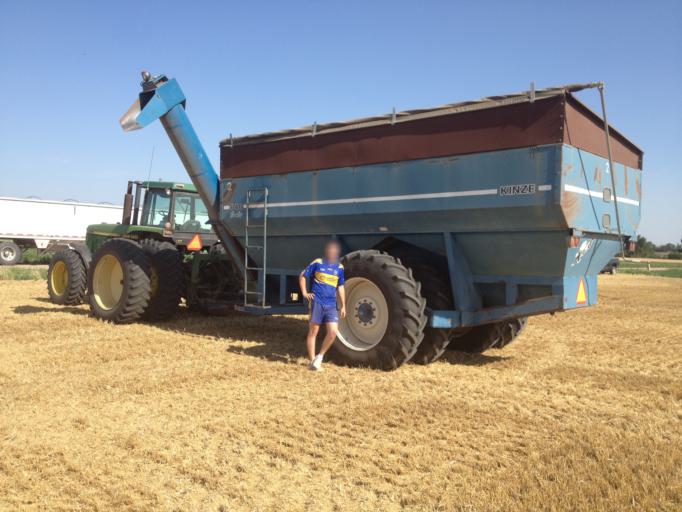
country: US
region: Kansas
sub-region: Rice County
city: Lyons
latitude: 38.3648
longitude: -98.3698
